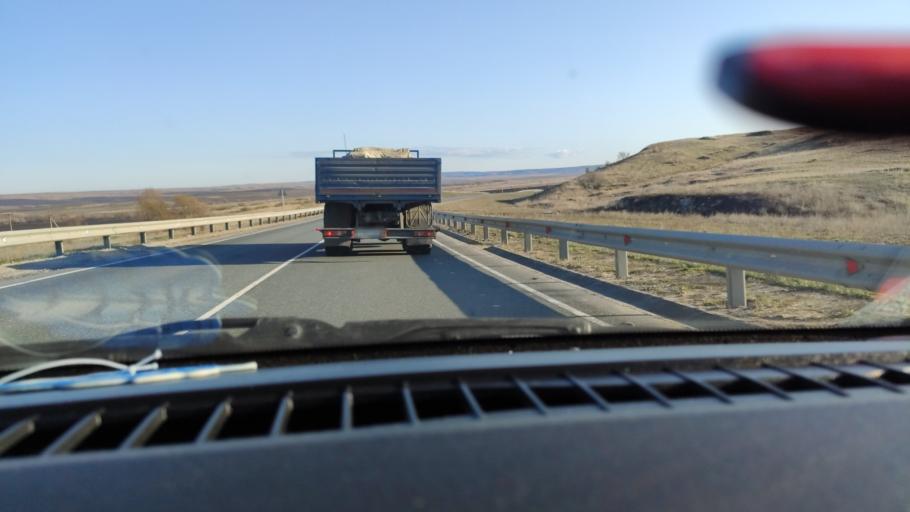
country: RU
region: Saratov
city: Alekseyevka
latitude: 52.3276
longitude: 47.9203
